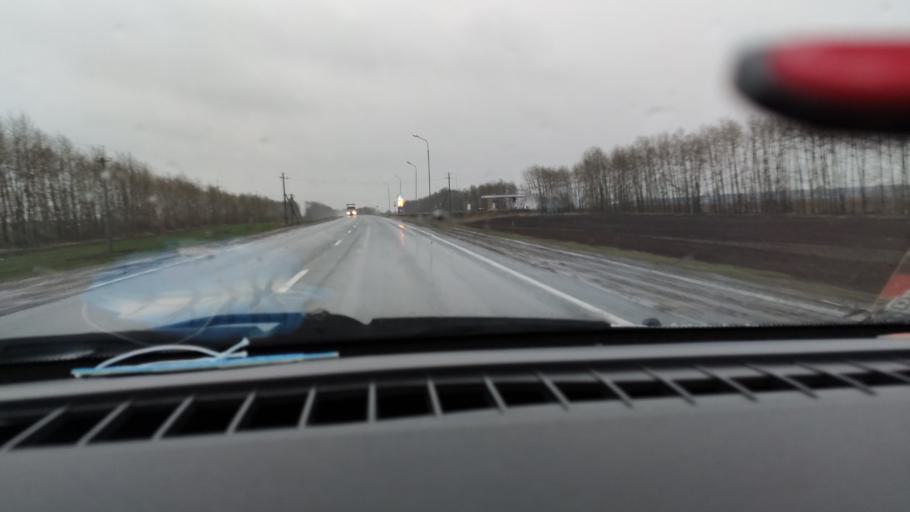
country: RU
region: Tatarstan
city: Mendeleyevsk
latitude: 55.9169
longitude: 52.2729
